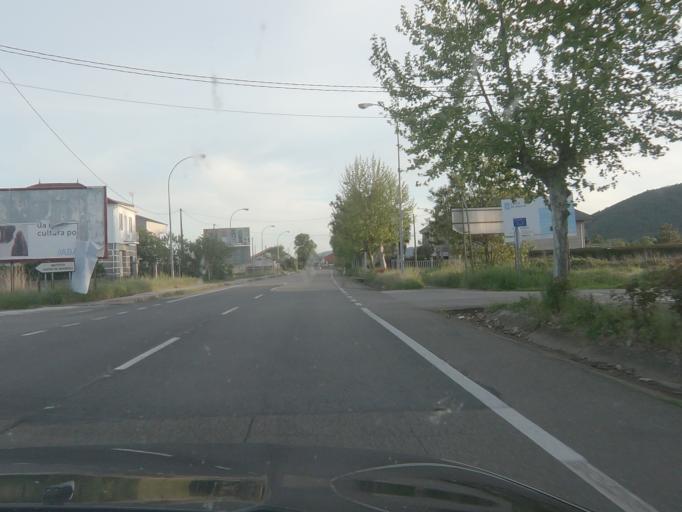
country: ES
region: Galicia
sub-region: Provincia de Ourense
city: Verin
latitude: 41.9263
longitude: -7.4419
